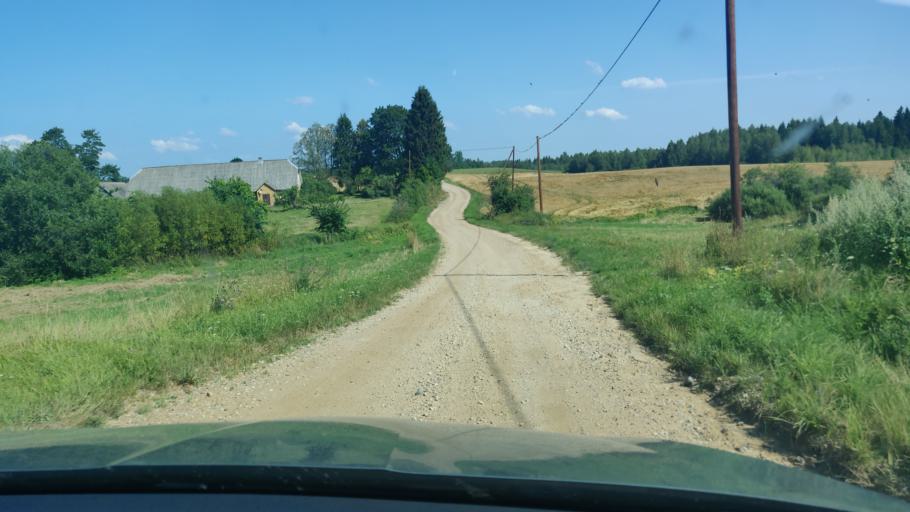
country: EE
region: Tartu
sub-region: Elva linn
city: Elva
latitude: 58.1203
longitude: 26.4602
